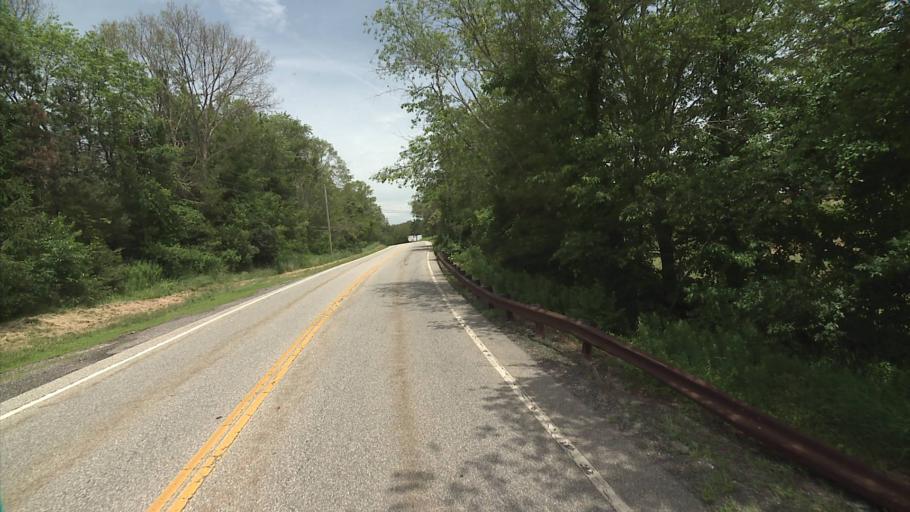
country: US
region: Connecticut
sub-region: New London County
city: Preston City
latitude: 41.5549
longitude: -71.9702
